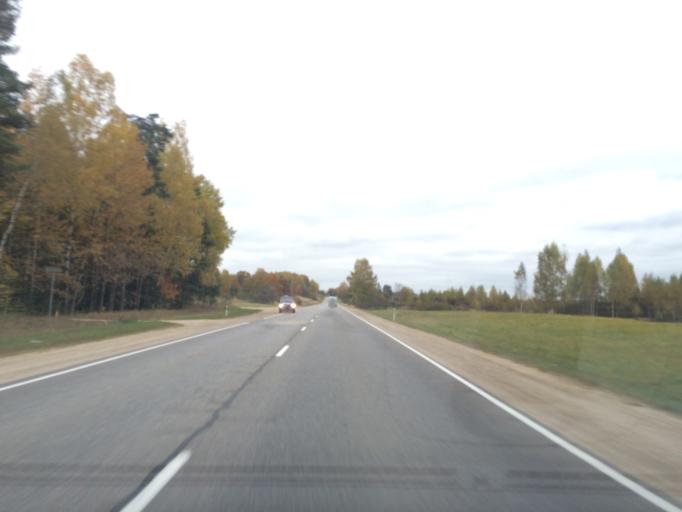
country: LV
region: Koknese
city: Koknese
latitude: 56.5965
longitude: 25.5346
